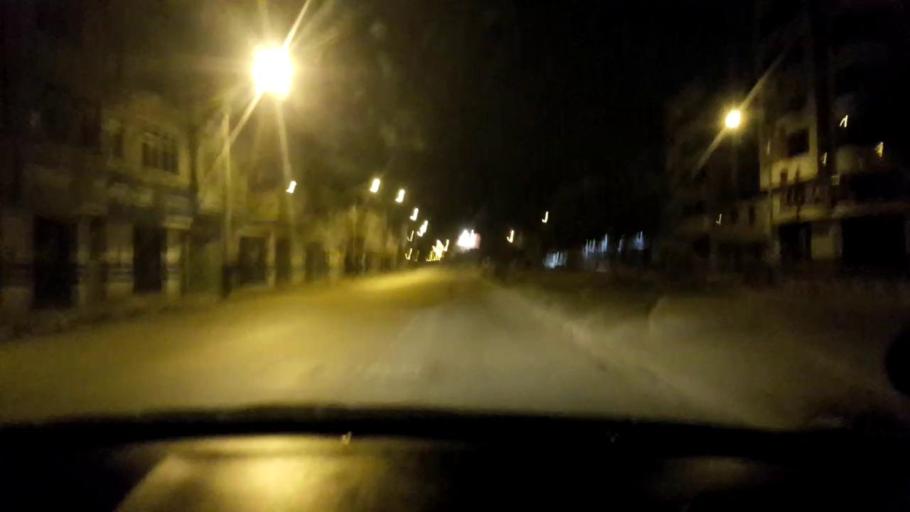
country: PE
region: Lambayeque
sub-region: Provincia de Chiclayo
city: Santa Rosa
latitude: -6.7626
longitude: -79.8379
